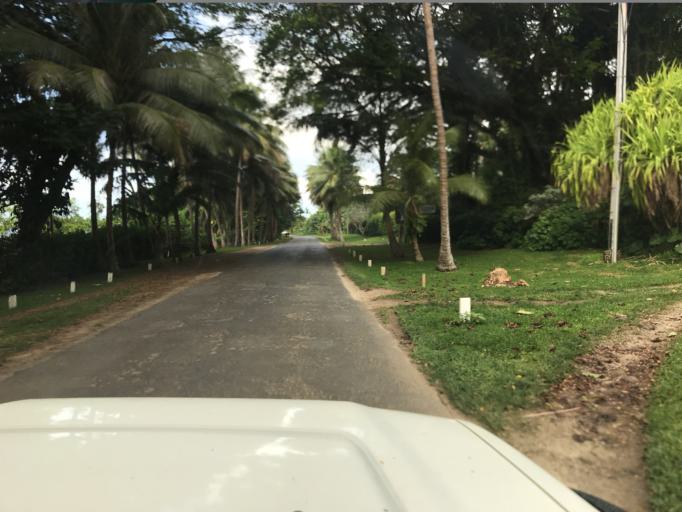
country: VU
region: Sanma
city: Luganville
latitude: -15.5402
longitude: 167.1516
